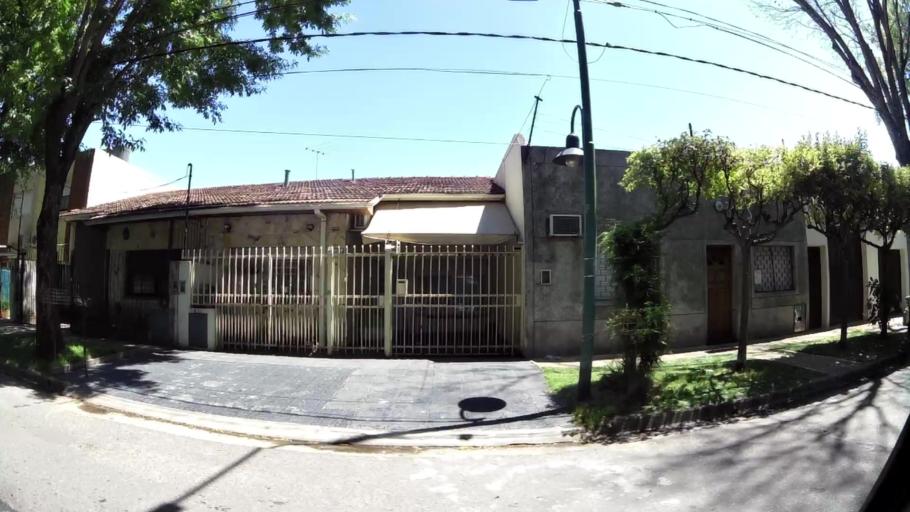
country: AR
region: Buenos Aires
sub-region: Partido de Vicente Lopez
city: Olivos
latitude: -34.5110
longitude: -58.5177
